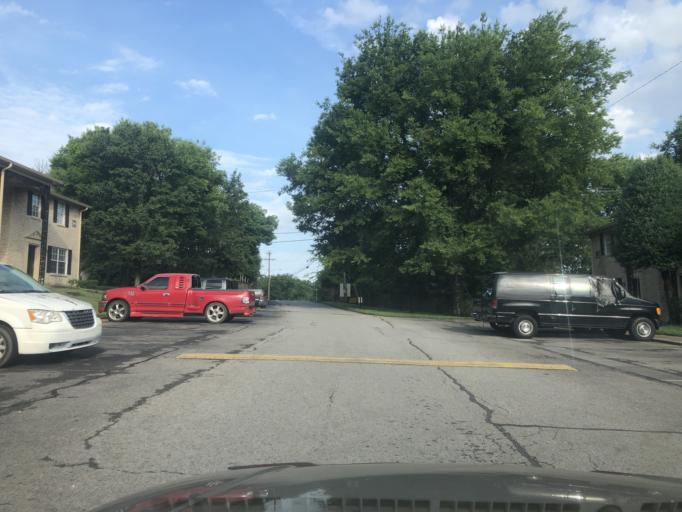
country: US
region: Tennessee
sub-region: Davidson County
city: Goodlettsville
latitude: 36.2466
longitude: -86.7145
